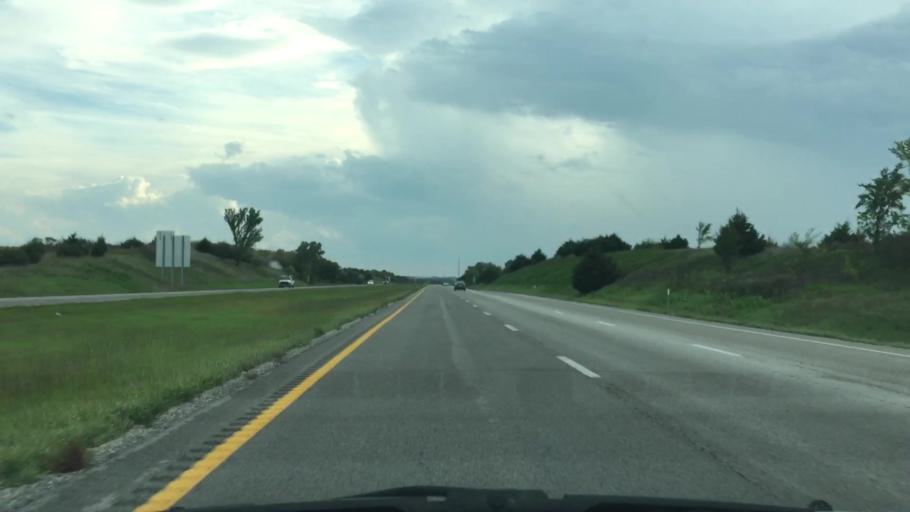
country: US
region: Missouri
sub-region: Clinton County
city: Cameron
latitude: 39.8969
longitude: -94.1531
